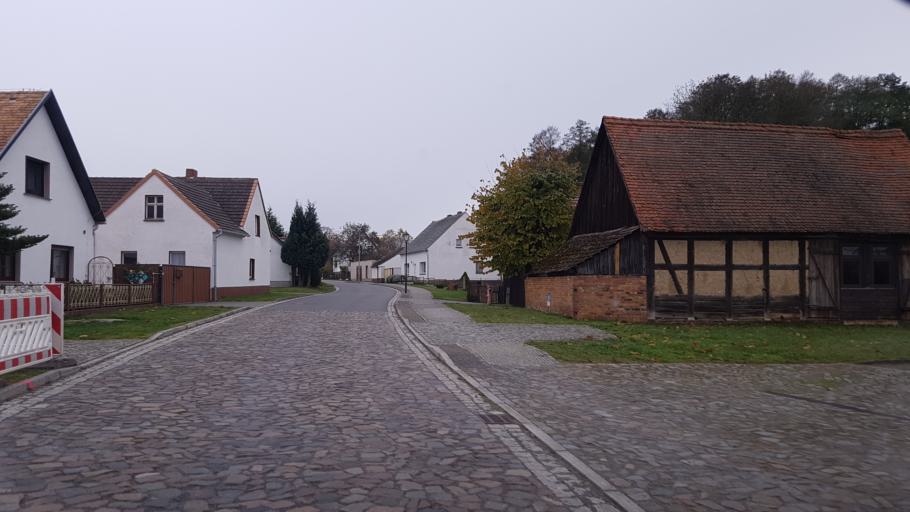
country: DE
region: Brandenburg
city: Crinitz
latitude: 51.7576
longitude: 13.8054
